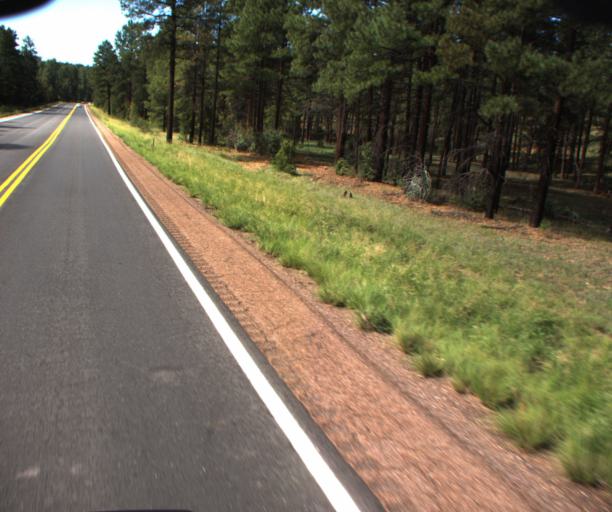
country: US
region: Arizona
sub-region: Navajo County
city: Show Low
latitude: 34.1893
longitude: -110.0916
